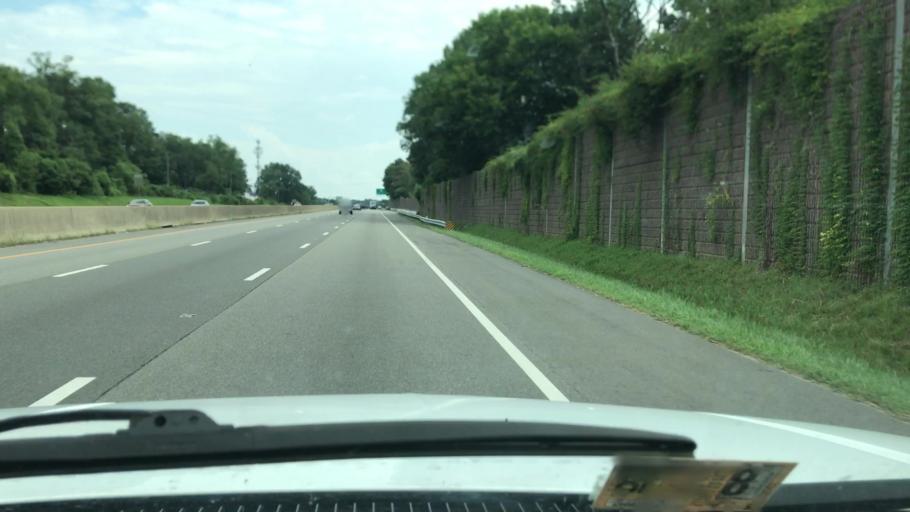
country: US
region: Virginia
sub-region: Chesterfield County
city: Bon Air
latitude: 37.4853
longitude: -77.5182
